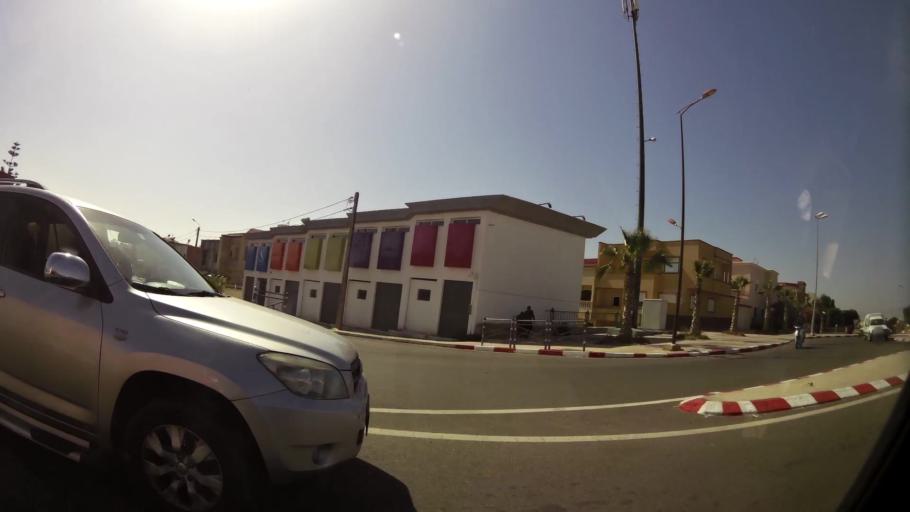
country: MA
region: Souss-Massa-Draa
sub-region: Inezgane-Ait Mellou
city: Inezgane
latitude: 30.3643
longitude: -9.5452
